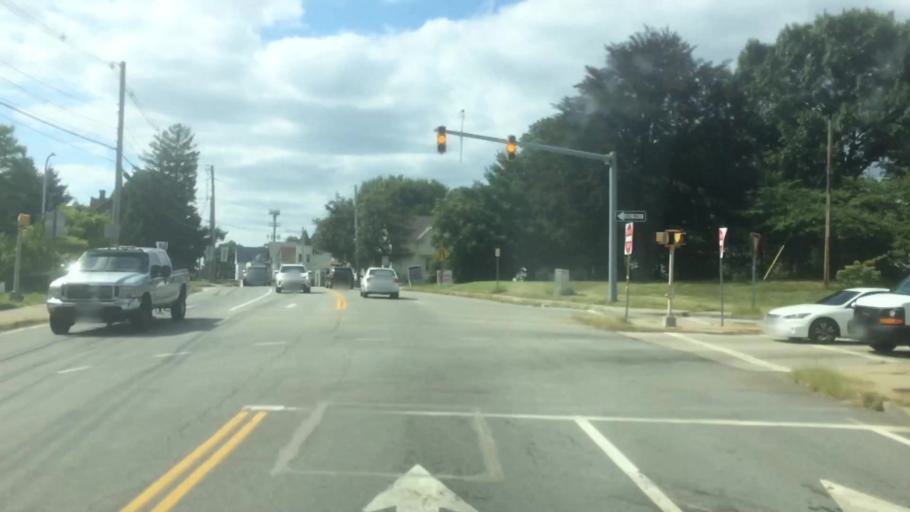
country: US
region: Rhode Island
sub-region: Providence County
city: Cranston
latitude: 41.7753
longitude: -71.4174
